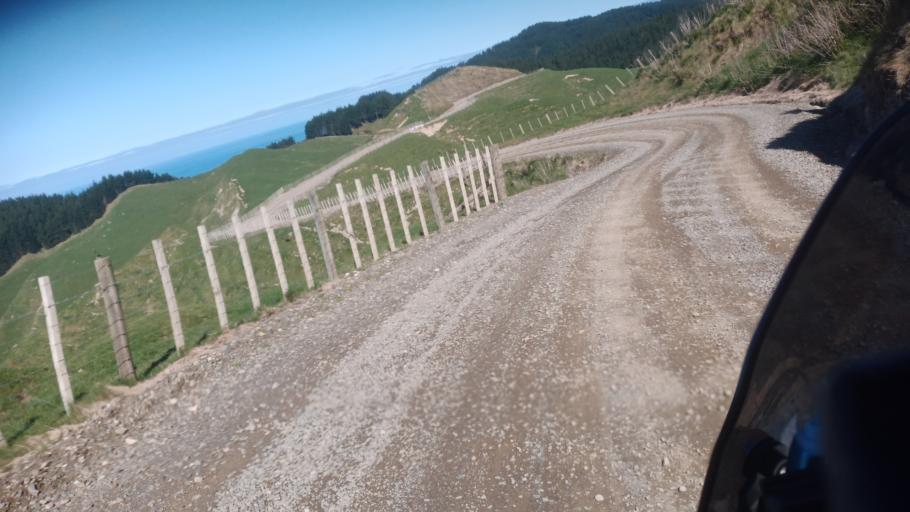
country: NZ
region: Gisborne
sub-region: Gisborne District
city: Gisborne
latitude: -39.1678
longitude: 177.8981
